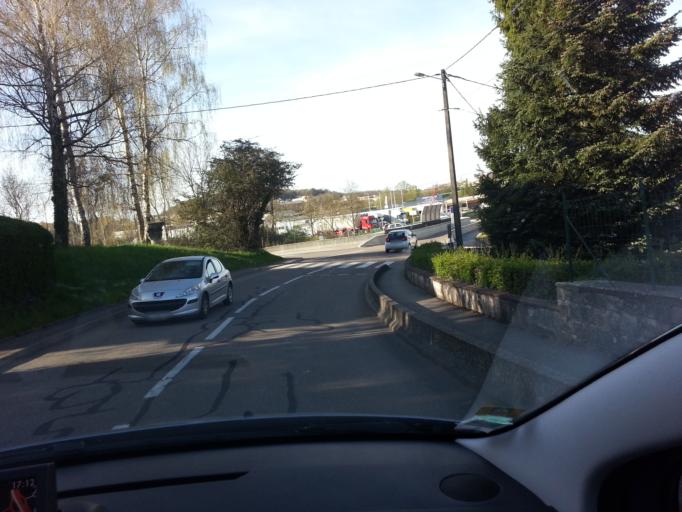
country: FR
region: Franche-Comte
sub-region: Departement du Doubs
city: Miserey-Salines
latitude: 47.2750
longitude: 5.9896
